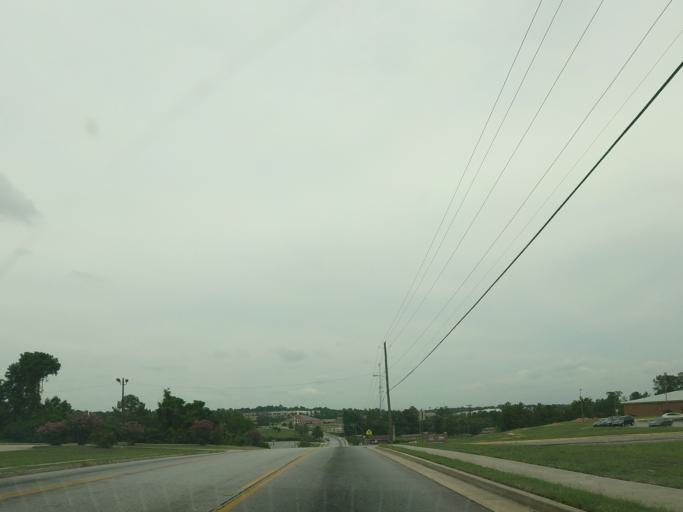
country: US
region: Georgia
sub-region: Bibb County
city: Macon
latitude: 32.8220
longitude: -83.6789
